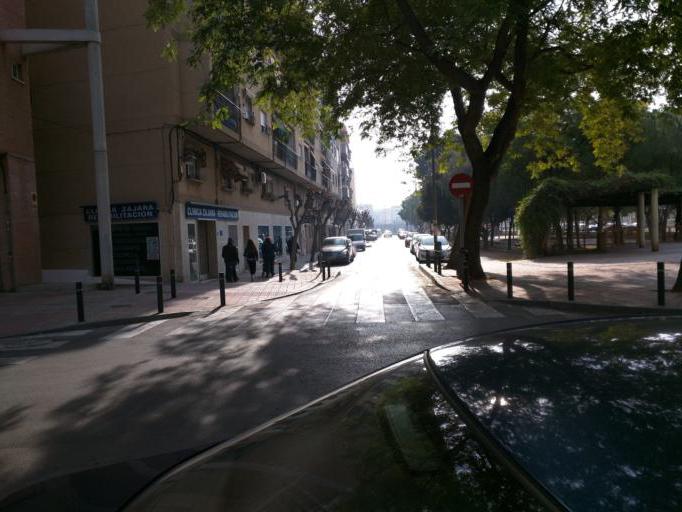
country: ES
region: Murcia
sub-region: Murcia
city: Murcia
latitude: 37.9880
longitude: -1.1405
